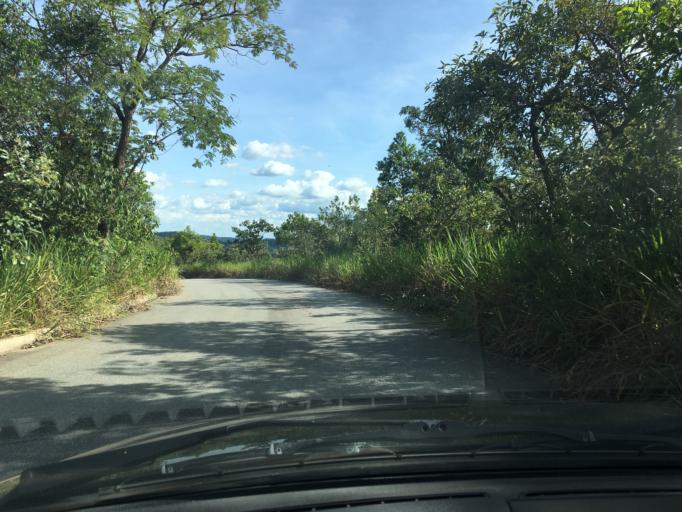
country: BR
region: Minas Gerais
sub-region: Ibirite
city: Ibirite
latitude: -20.1290
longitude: -44.0705
